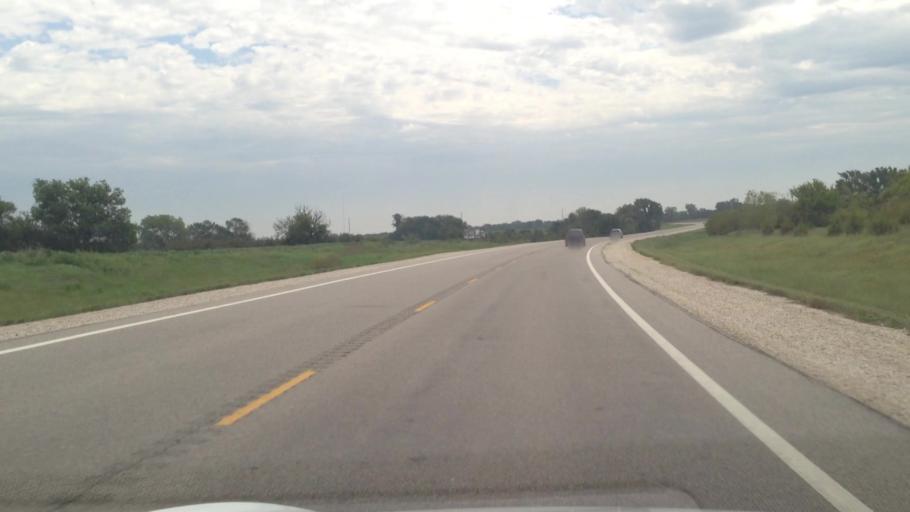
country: US
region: Kansas
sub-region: Allen County
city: Iola
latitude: 37.9201
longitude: -95.1581
